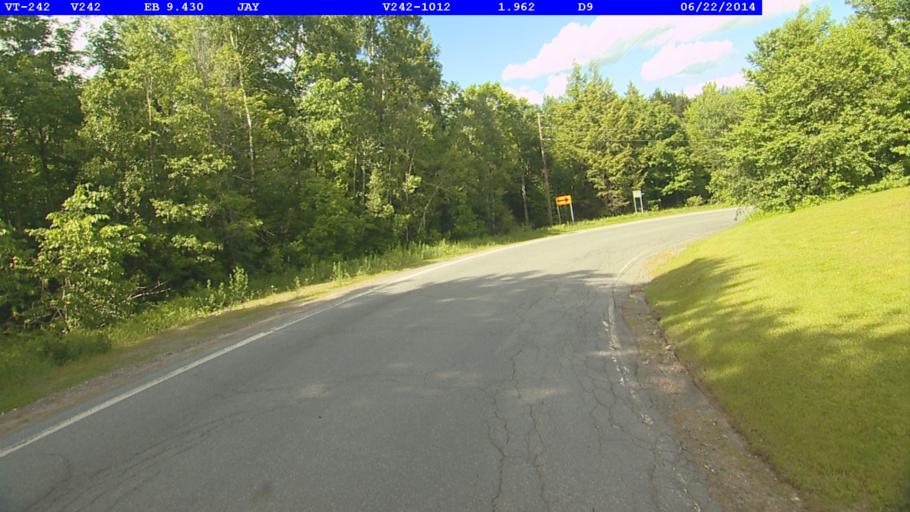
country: US
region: Vermont
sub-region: Franklin County
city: Richford
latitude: 44.9412
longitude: -72.4746
